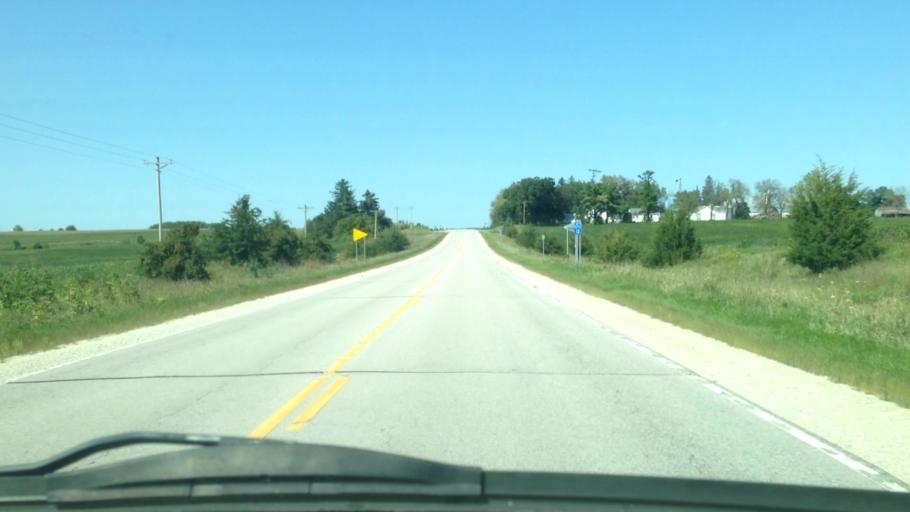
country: US
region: Minnesota
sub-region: Houston County
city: Spring Grove
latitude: 43.6239
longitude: -91.7903
